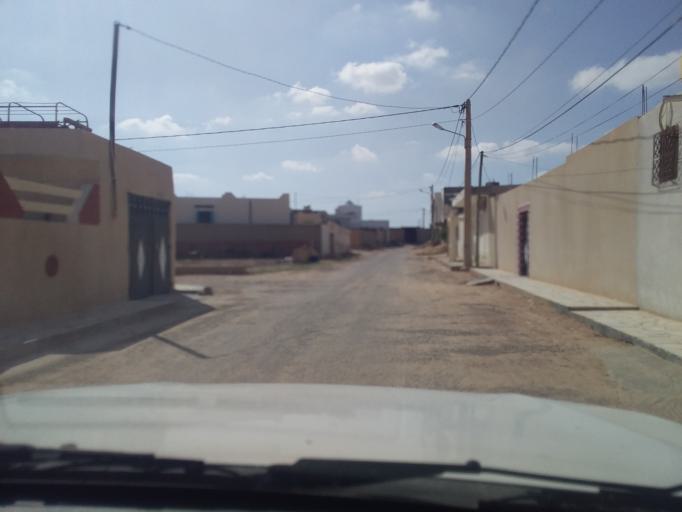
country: TN
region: Madanin
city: Medenine
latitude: 33.5813
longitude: 10.3231
